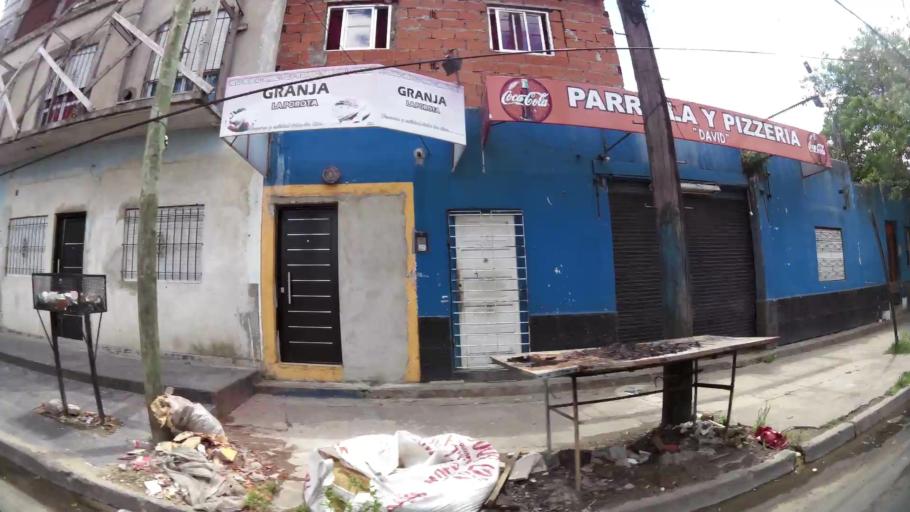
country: AR
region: Buenos Aires
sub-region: Partido de Lanus
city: Lanus
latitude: -34.7022
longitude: -58.4277
